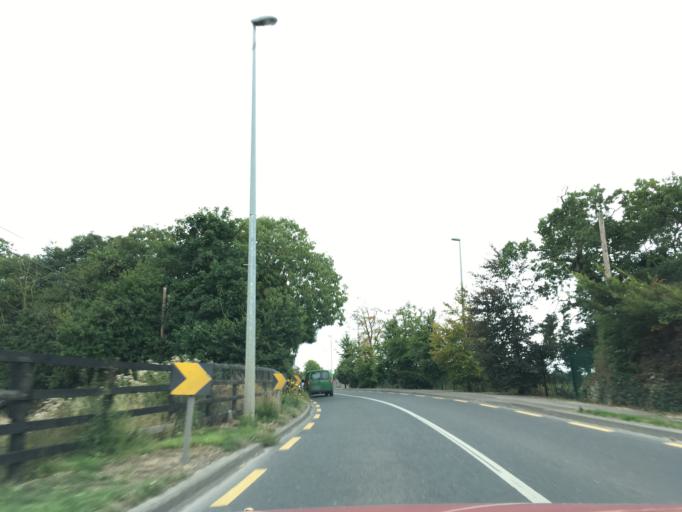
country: IE
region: Munster
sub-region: South Tipperary
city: Cluain Meala
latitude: 52.4116
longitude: -7.7513
